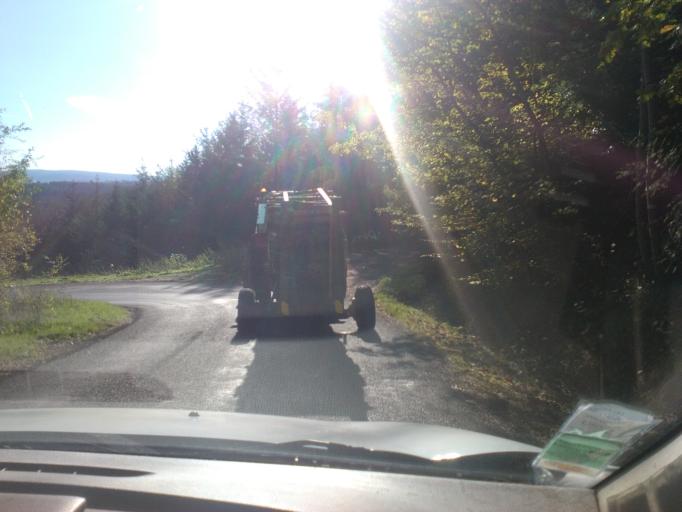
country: FR
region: Lorraine
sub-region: Departement des Vosges
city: Taintrux
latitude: 48.2280
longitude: 6.8835
